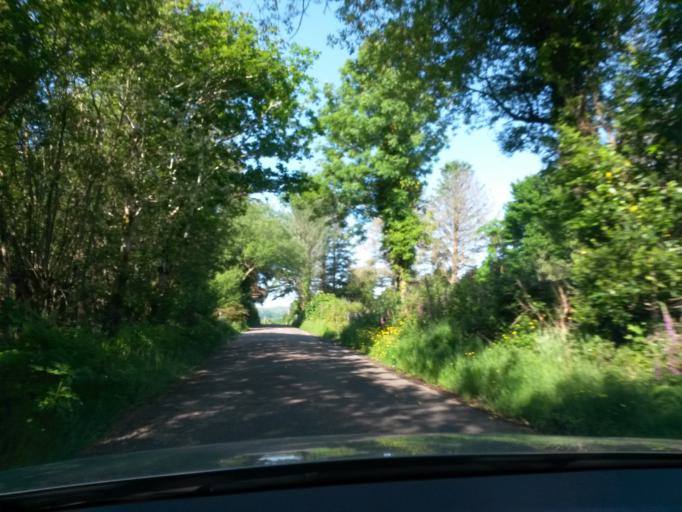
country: IE
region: Munster
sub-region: Ciarrai
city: Kenmare
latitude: 51.8041
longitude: -9.7549
